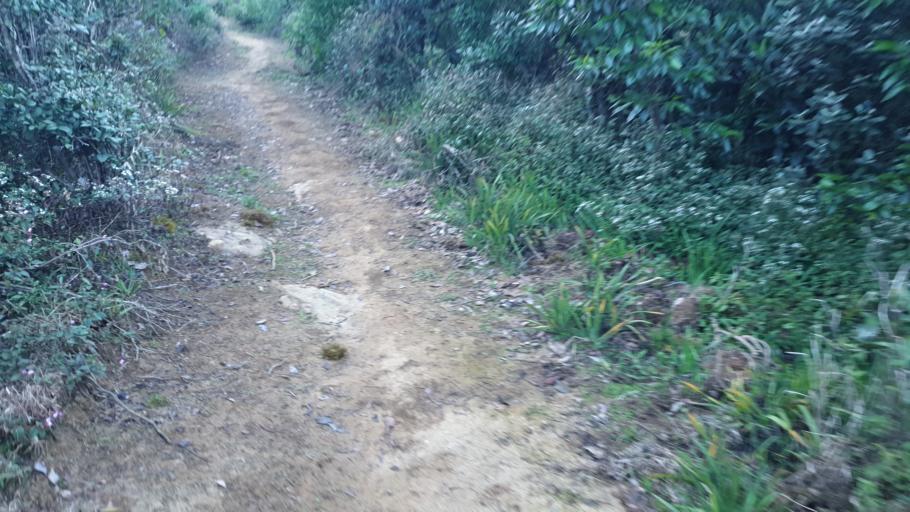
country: LK
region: Central
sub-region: Nuwara Eliya District
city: Nuwara Eliya
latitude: 6.9593
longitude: 80.7620
